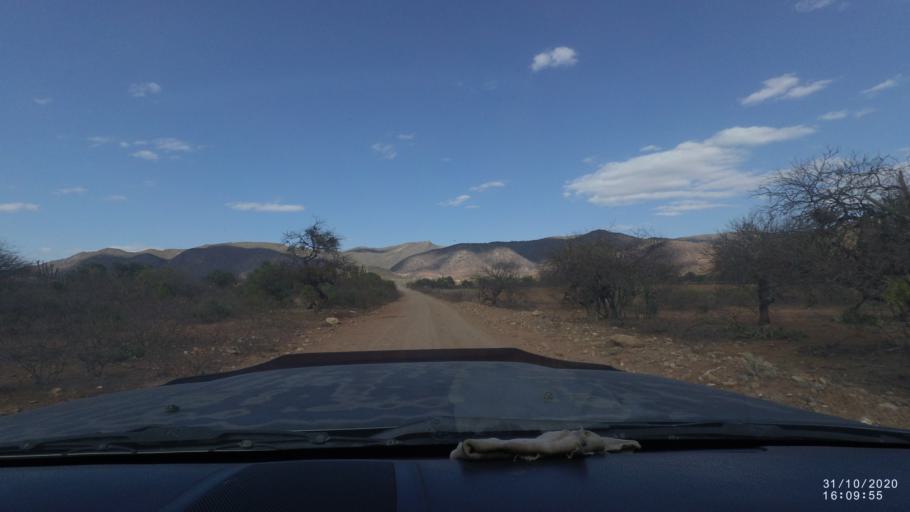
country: BO
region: Chuquisaca
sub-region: Provincia Zudanez
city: Mojocoya
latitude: -18.3847
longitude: -64.6340
